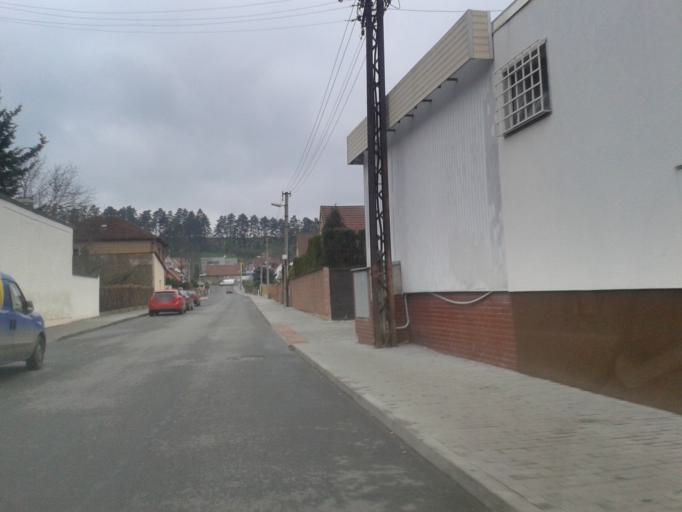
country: CZ
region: Central Bohemia
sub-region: Okres Beroun
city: Kraluv Dvur
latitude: 49.9424
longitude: 14.0270
